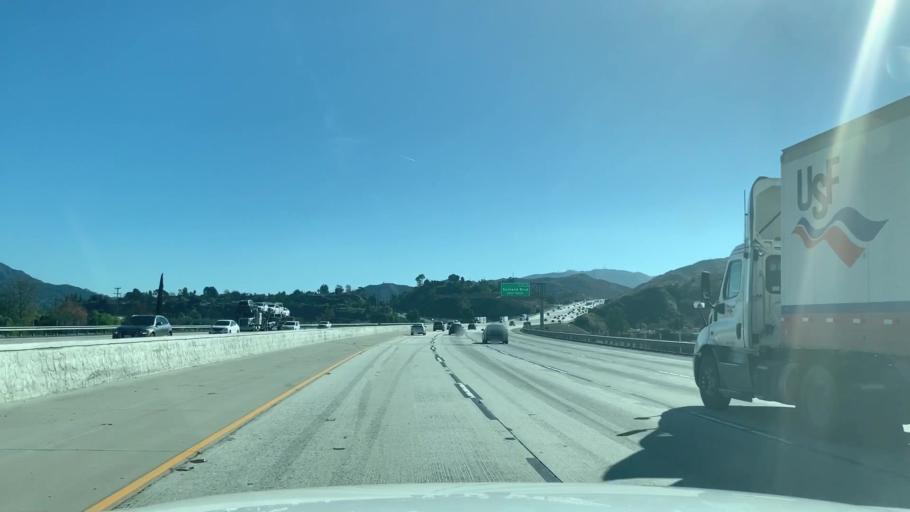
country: US
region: California
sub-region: Los Angeles County
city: Burbank
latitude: 34.2692
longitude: -118.3397
